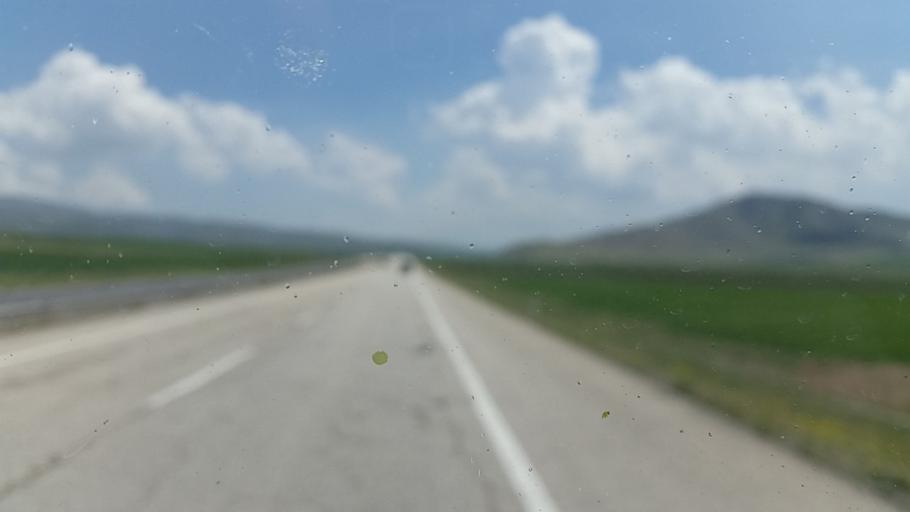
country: TR
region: Agri
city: Taslicay
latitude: 39.6245
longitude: 43.4702
